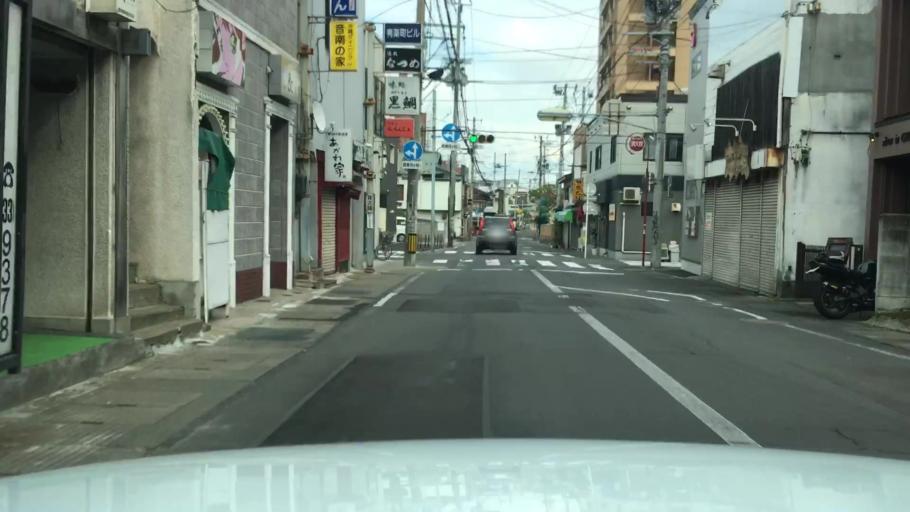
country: JP
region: Aomori
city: Hirosaki
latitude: 40.6002
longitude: 140.4706
